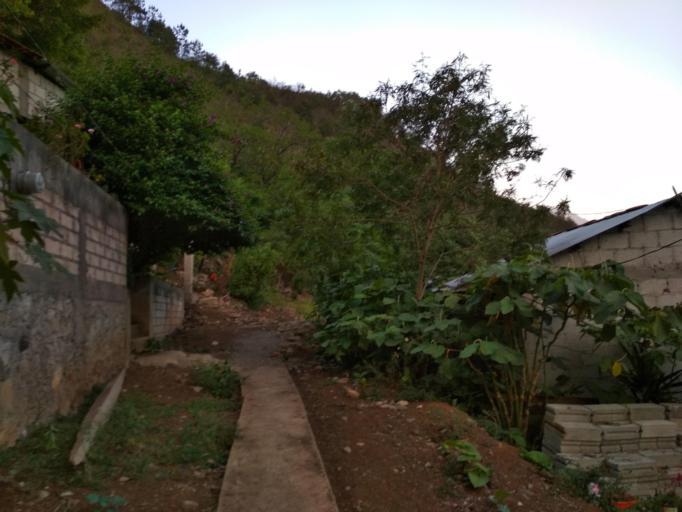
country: MX
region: Veracruz
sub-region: Nogales
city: Taza de Agua Ojo Zarco
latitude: 18.7740
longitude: -97.1892
